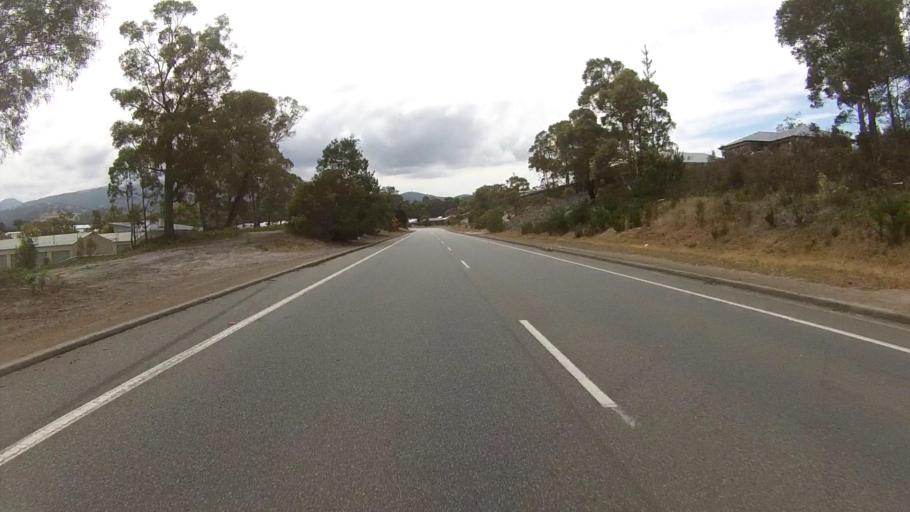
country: AU
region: Tasmania
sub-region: Kingborough
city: Kingston
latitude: -42.9921
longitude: 147.2944
